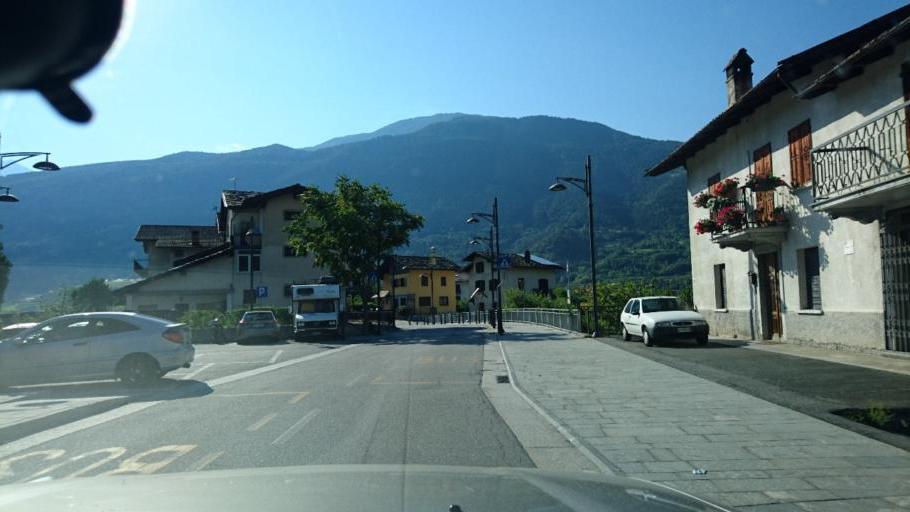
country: IT
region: Aosta Valley
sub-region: Valle d'Aosta
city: Saint-Pierre
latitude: 45.7089
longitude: 7.2348
